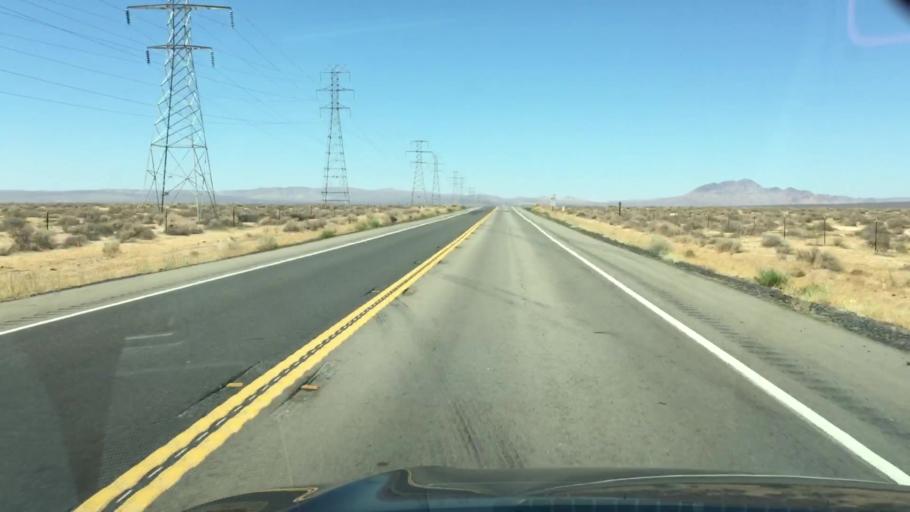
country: US
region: California
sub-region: Kern County
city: Boron
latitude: 35.1600
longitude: -117.5883
